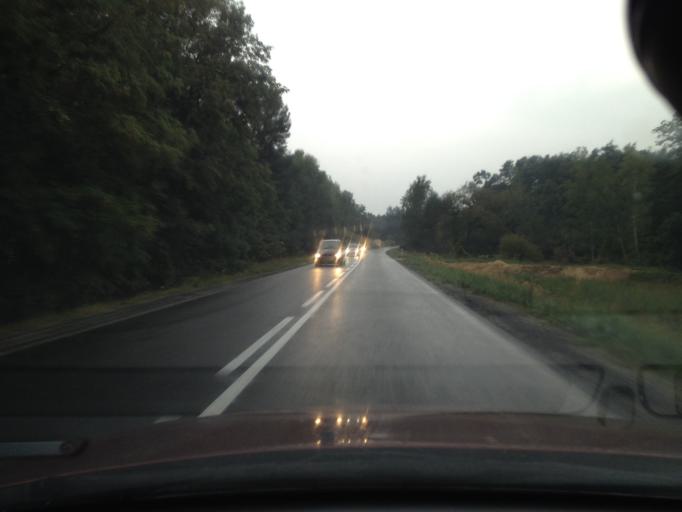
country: PL
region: Lubusz
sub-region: Powiat zaganski
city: Zagan
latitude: 51.5724
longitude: 15.2707
